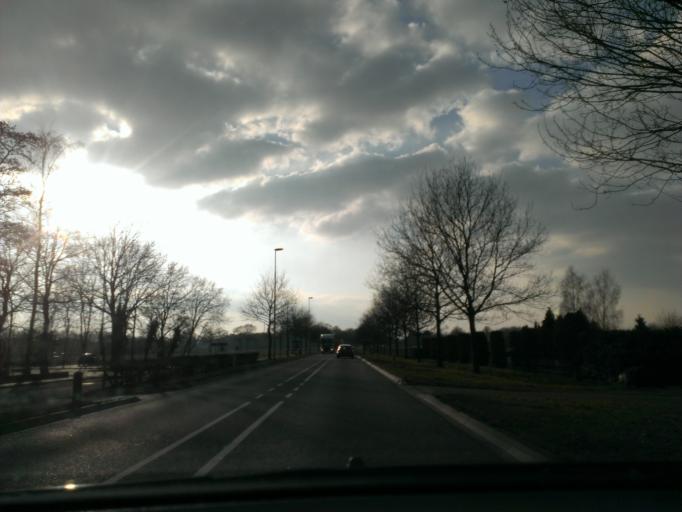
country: NL
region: Overijssel
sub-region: Gemeente Raalte
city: Raalte
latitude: 52.3814
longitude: 6.3193
